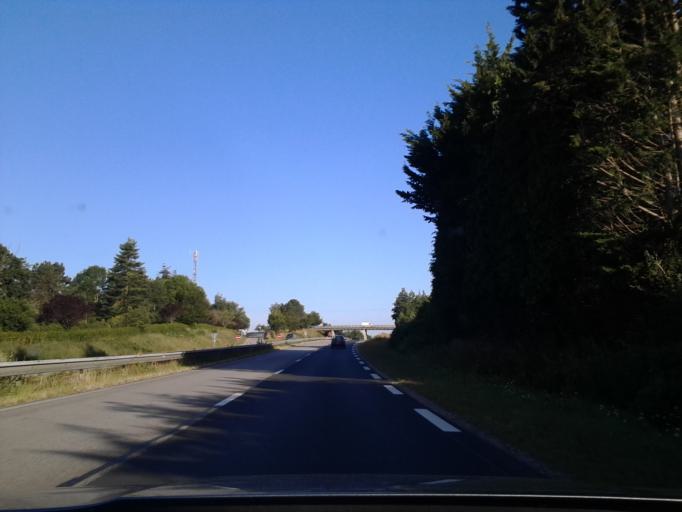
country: FR
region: Lower Normandy
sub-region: Departement de la Manche
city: Brix
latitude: 49.5325
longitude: -1.5282
